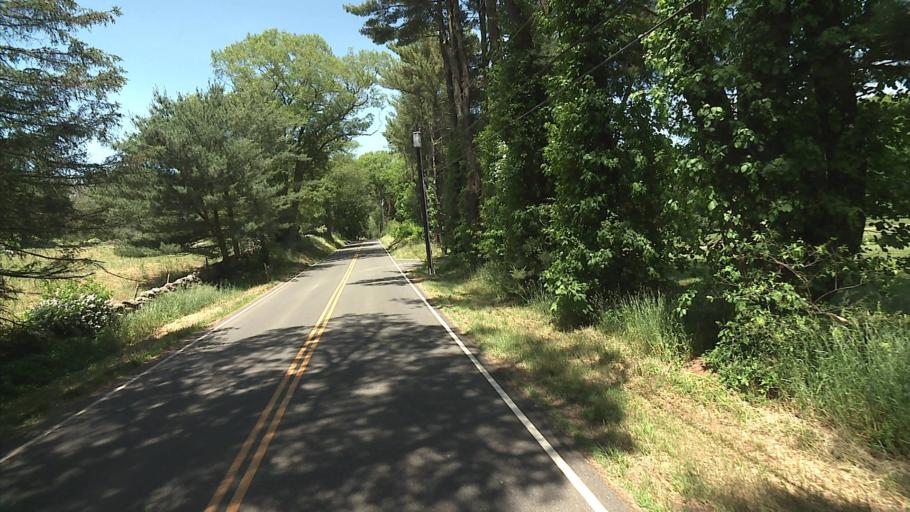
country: US
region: Rhode Island
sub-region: Washington County
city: Hopkinton
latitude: 41.4504
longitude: -71.8088
